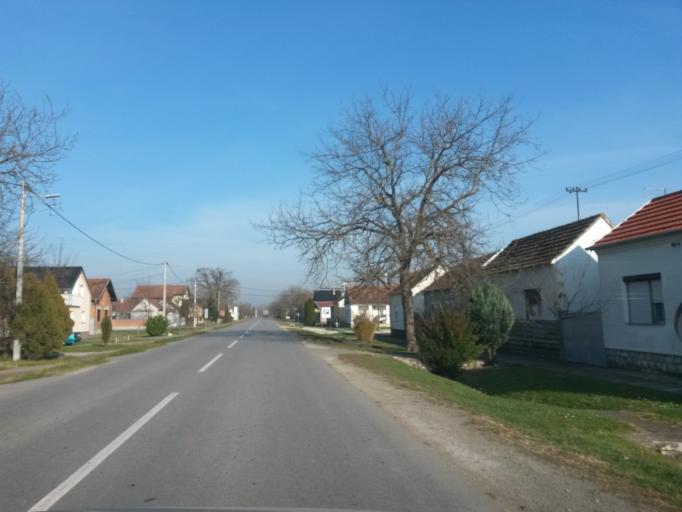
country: HR
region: Vukovarsko-Srijemska
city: Privlaka
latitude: 45.2030
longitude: 18.8483
